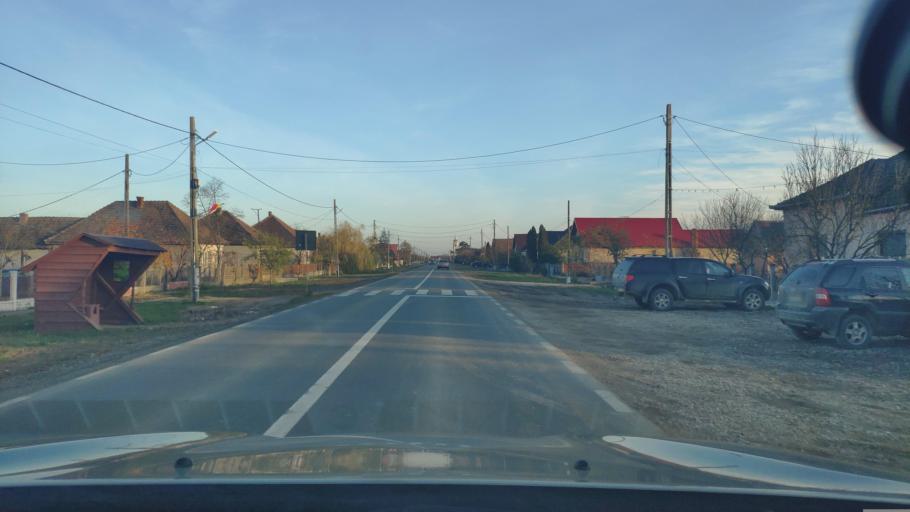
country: RO
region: Satu Mare
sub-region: Comuna Culciu
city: Caraseu
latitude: 47.7791
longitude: 23.0879
